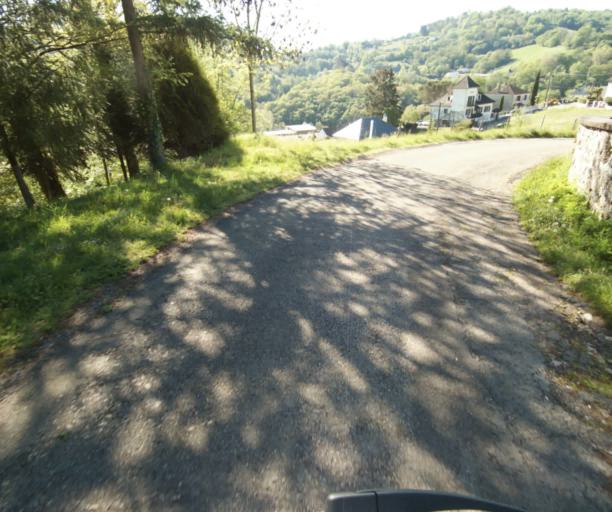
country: FR
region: Limousin
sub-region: Departement de la Correze
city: Tulle
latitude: 45.2797
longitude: 1.7790
